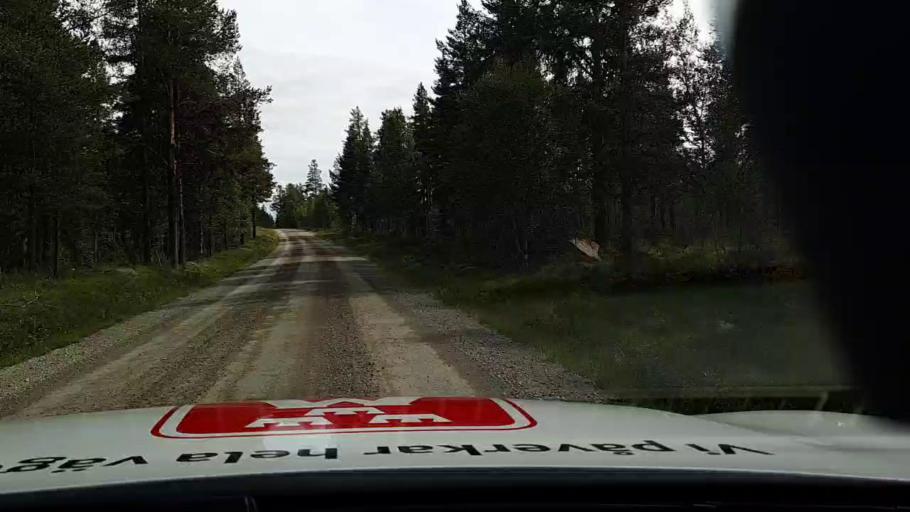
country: SE
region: Jaemtland
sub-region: Are Kommun
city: Jarpen
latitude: 62.5138
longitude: 13.4888
